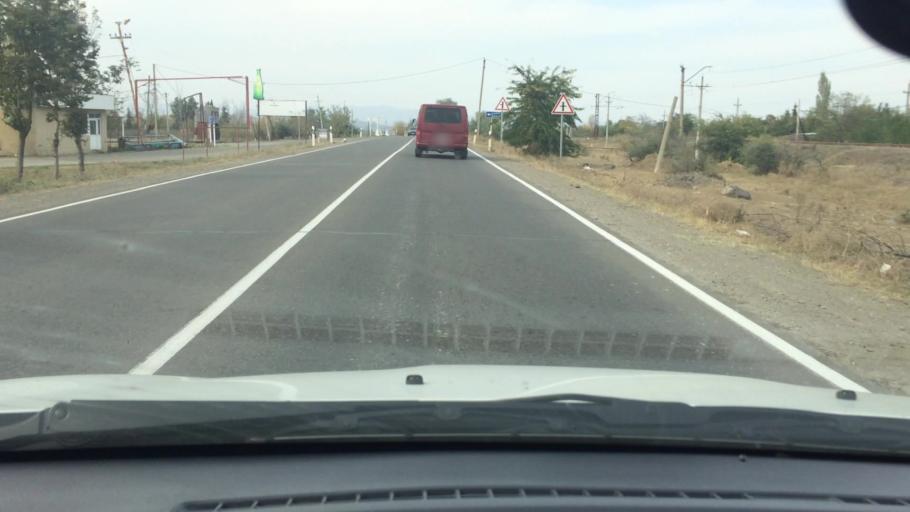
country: GE
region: Kvemo Kartli
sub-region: Marneuli
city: Marneuli
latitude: 41.4380
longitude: 44.8183
